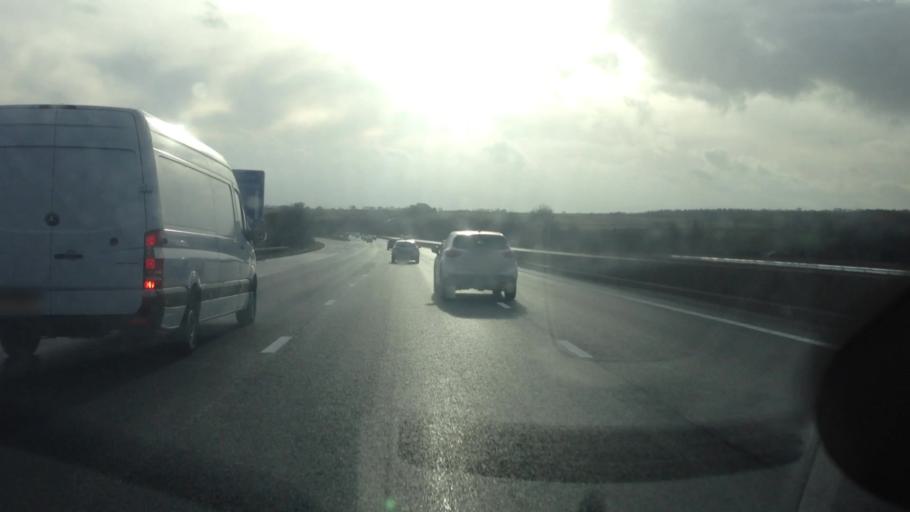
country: GB
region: England
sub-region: Barnsley
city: Darton
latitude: 53.6088
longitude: -1.5531
